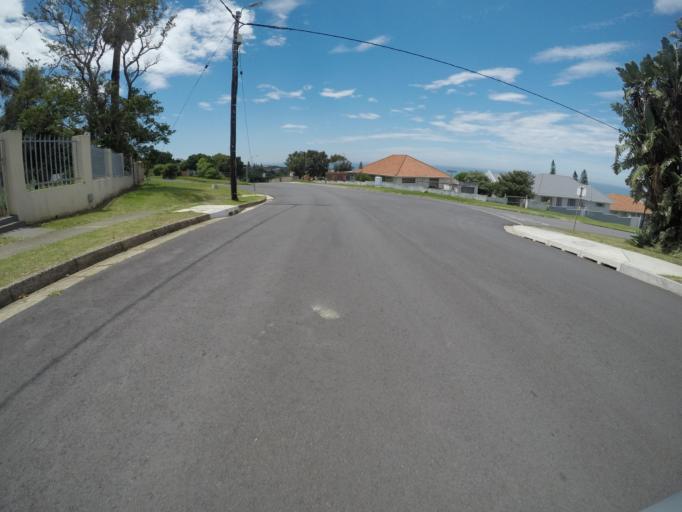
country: ZA
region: Eastern Cape
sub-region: Buffalo City Metropolitan Municipality
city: East London
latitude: -33.0372
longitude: 27.8564
